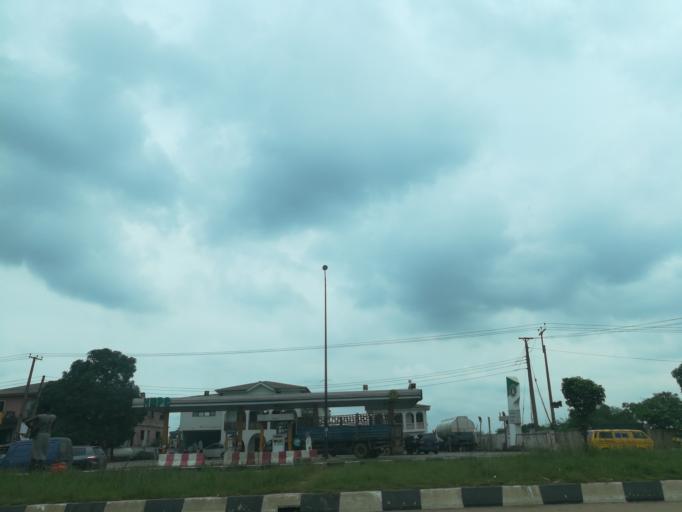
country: NG
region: Lagos
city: Ojota
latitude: 6.6112
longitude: 3.4192
